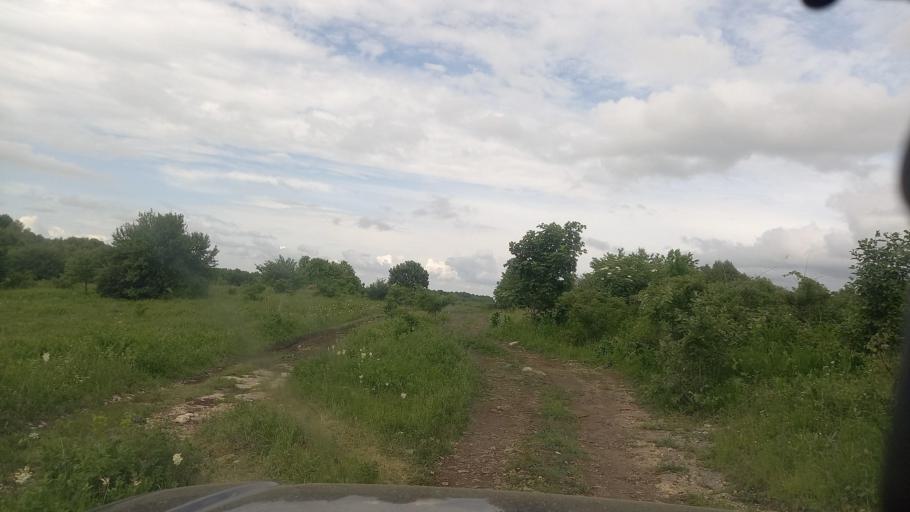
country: RU
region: Karachayevo-Cherkesiya
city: Pregradnaya
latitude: 44.0304
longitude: 41.3075
